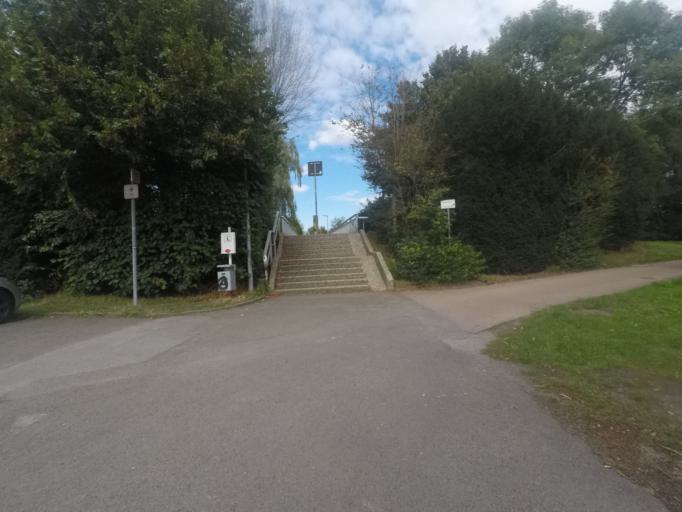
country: DE
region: North Rhine-Westphalia
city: Loehne
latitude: 52.2019
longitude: 8.7218
